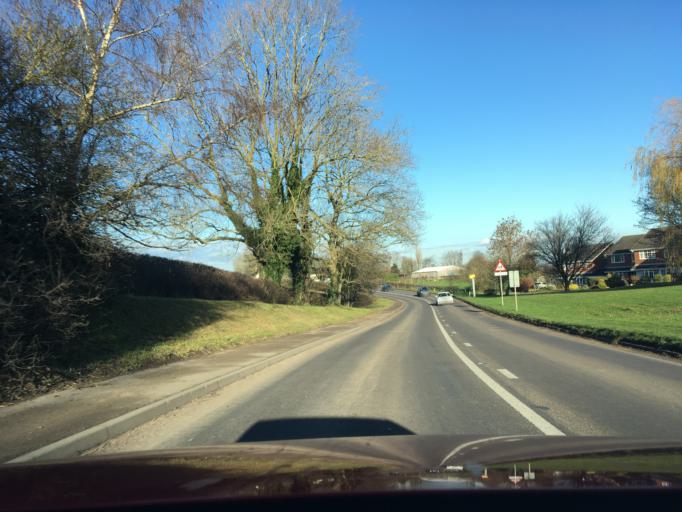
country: GB
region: England
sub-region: Staffordshire
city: Barton under Needwood
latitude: 52.8552
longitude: -1.7704
